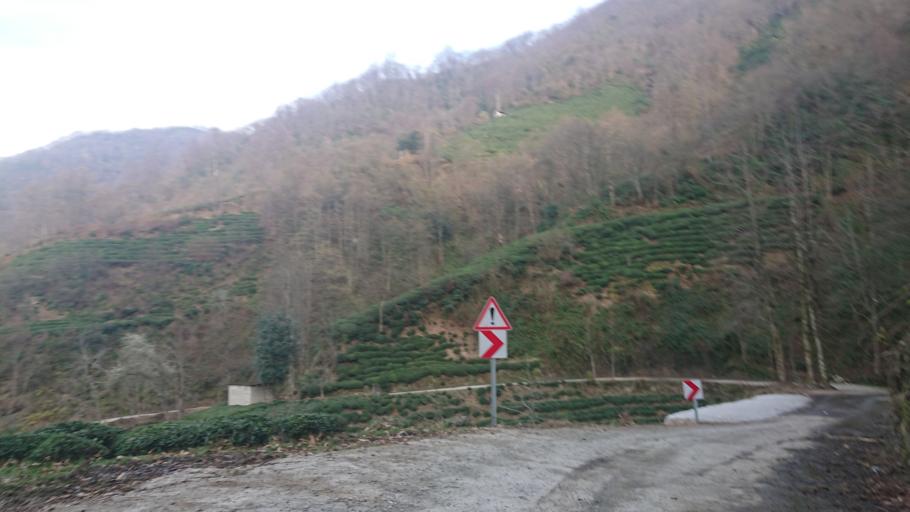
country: TR
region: Rize
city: Rize
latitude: 40.9770
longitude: 40.4955
